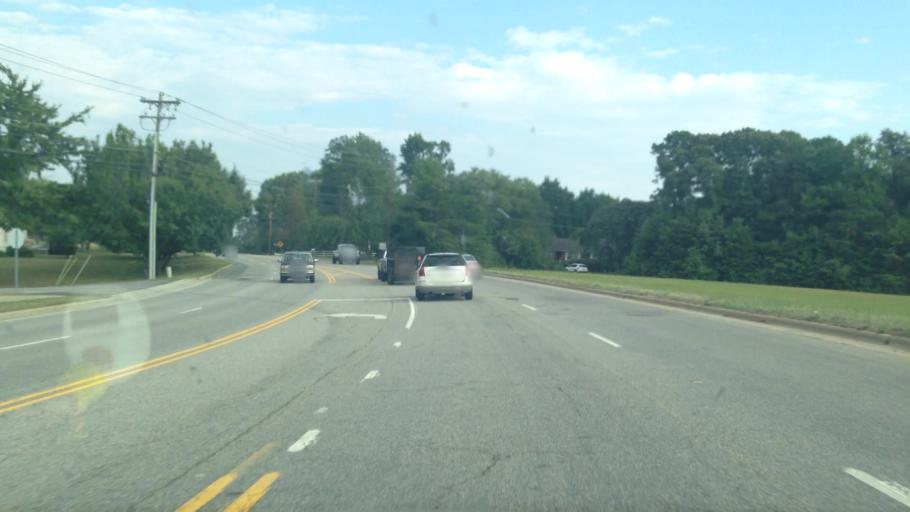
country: US
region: North Carolina
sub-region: Forsyth County
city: Kernersville
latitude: 36.0772
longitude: -80.0624
